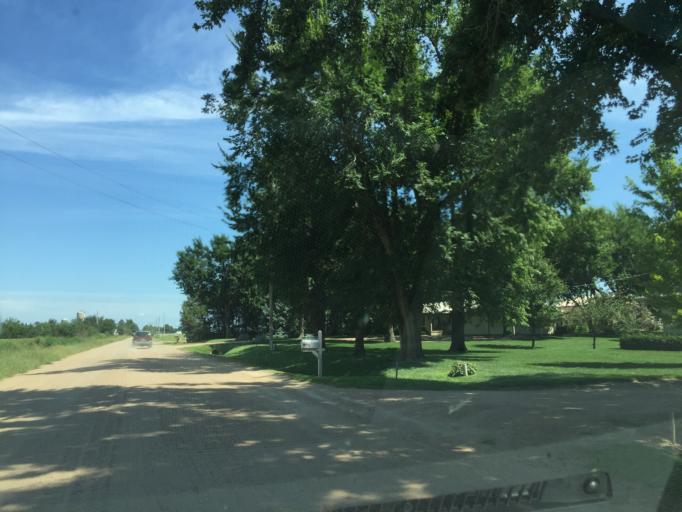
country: US
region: Kansas
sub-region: Reno County
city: South Hutchinson
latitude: 37.9853
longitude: -98.0319
